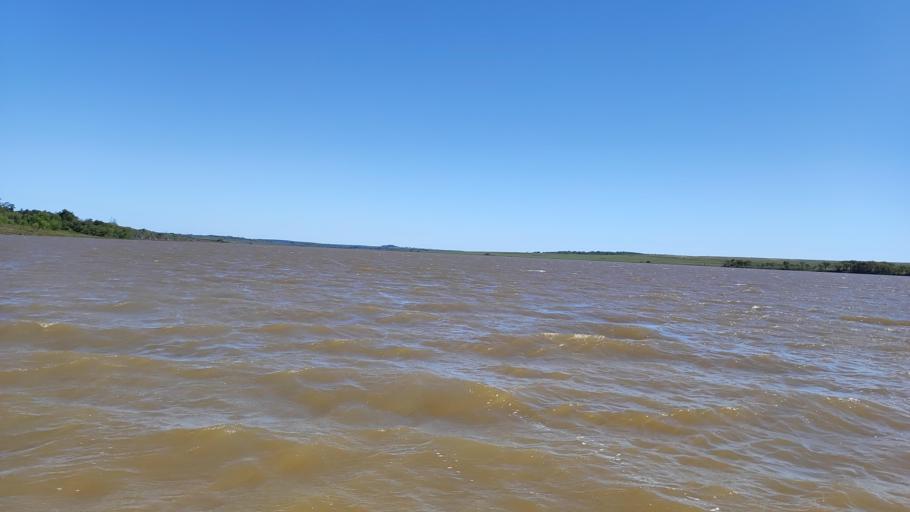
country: PY
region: Itapua
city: San Juan del Parana
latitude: -27.3474
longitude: -56.0371
